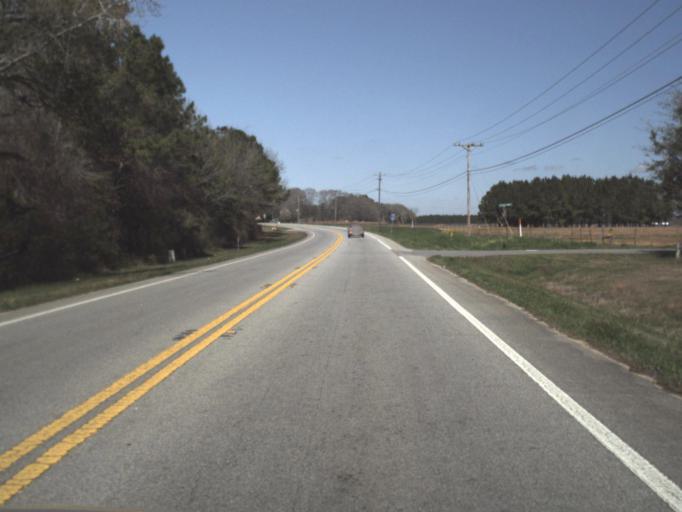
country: US
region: Florida
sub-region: Gadsden County
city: Quincy
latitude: 30.6479
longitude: -84.6008
